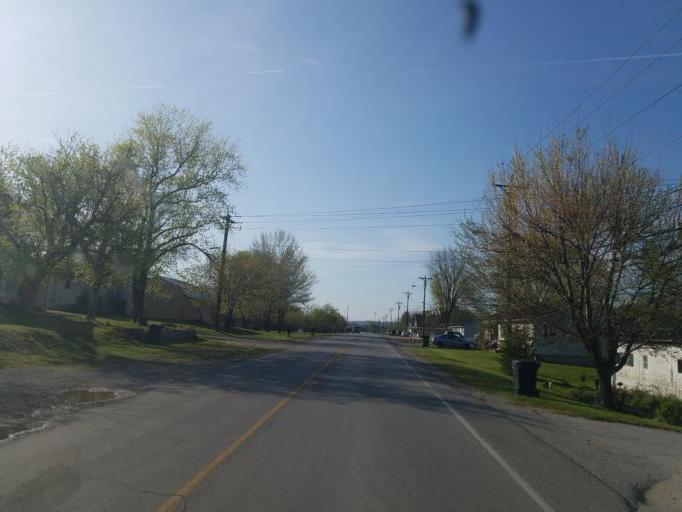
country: US
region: Kentucky
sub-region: Hart County
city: Munfordville
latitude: 37.3005
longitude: -85.9099
